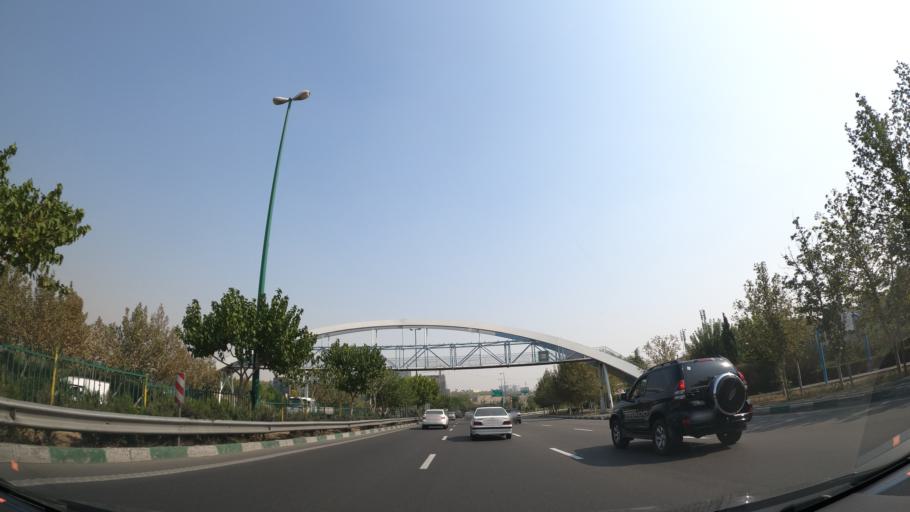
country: IR
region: Tehran
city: Shahr-e Qods
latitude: 35.7573
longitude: 51.2640
